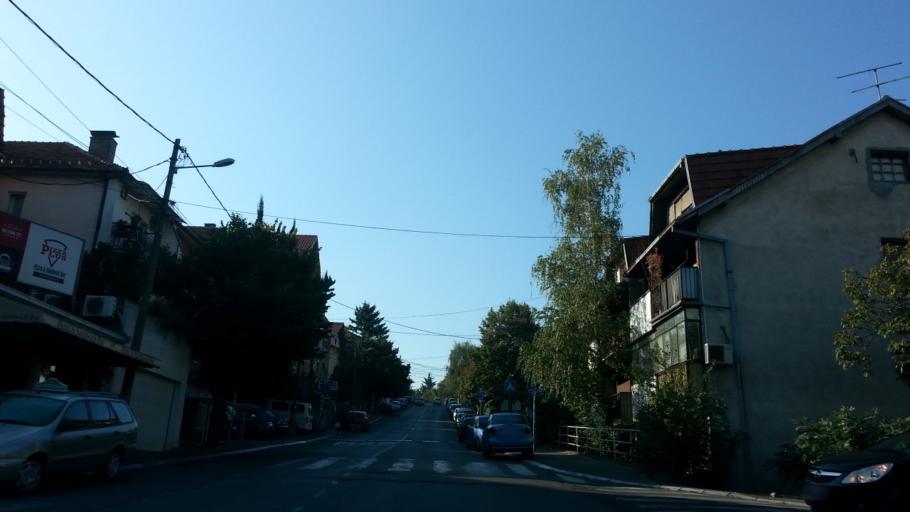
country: RS
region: Central Serbia
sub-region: Belgrade
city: Cukarica
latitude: 44.7642
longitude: 20.4191
